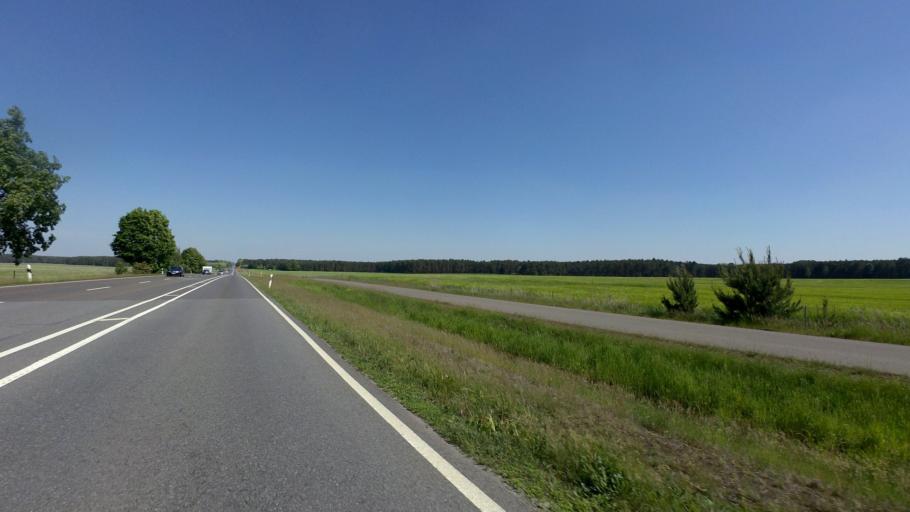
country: DE
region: Brandenburg
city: Spremberg
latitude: 51.6032
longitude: 14.3637
